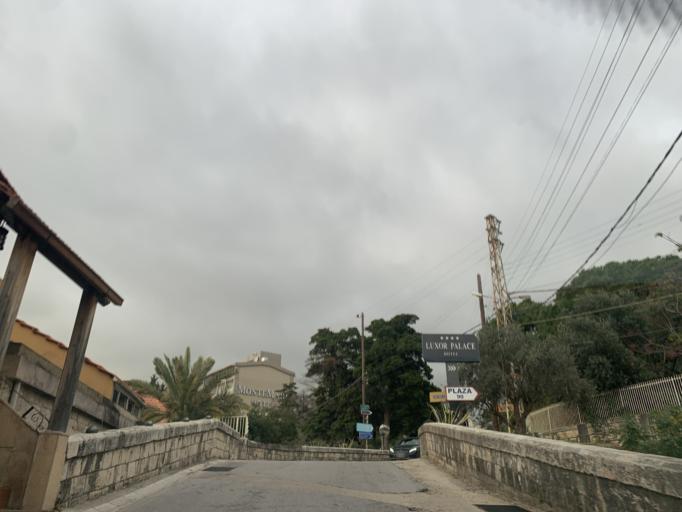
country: LB
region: Mont-Liban
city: Djounie
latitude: 34.0065
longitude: 35.6456
